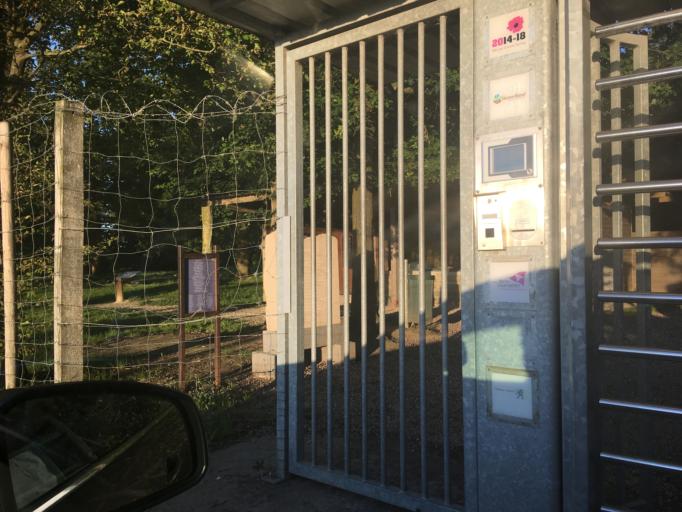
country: BE
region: Flanders
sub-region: Provincie West-Vlaanderen
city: Ieper
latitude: 50.8013
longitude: 2.8767
